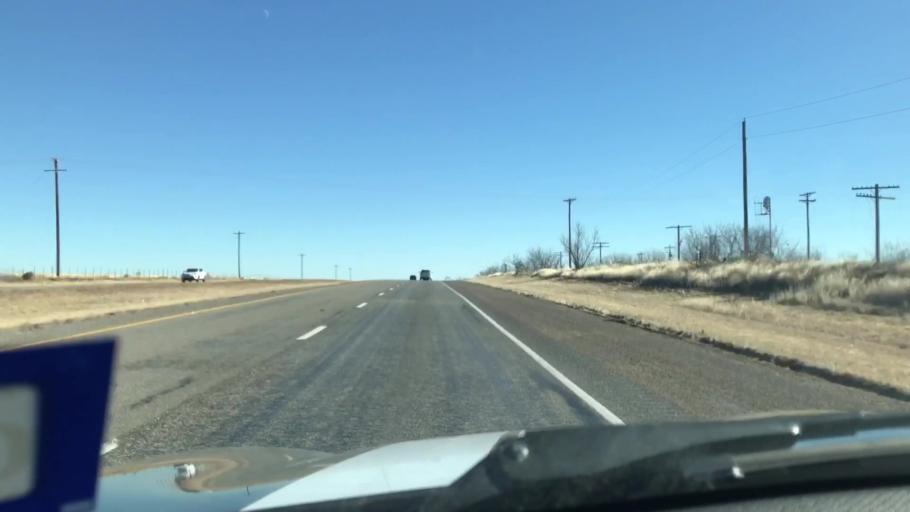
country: US
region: Texas
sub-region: Garza County
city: Post
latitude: 33.1353
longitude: -101.3081
